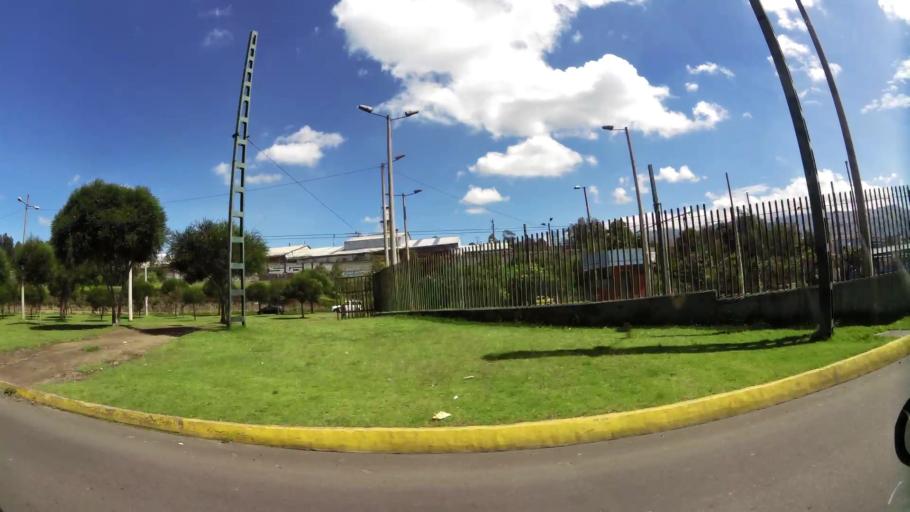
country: EC
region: Pichincha
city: Quito
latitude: -0.2846
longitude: -78.5449
